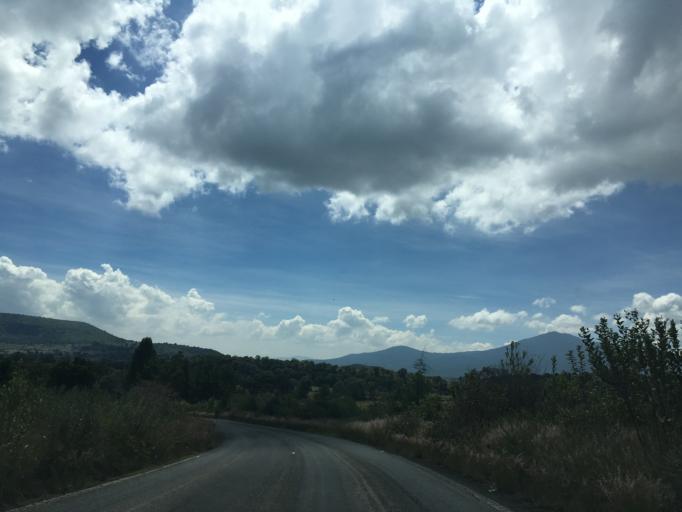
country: MX
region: Michoacan
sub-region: Morelia
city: Cuto de la Esperanza
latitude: 19.7310
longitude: -101.3488
